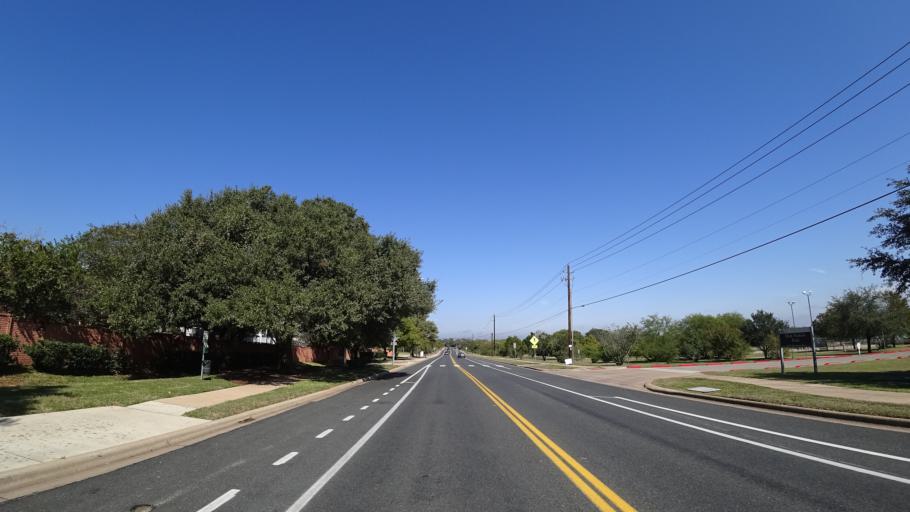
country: US
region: Texas
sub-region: Travis County
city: Shady Hollow
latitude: 30.2141
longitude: -97.8639
